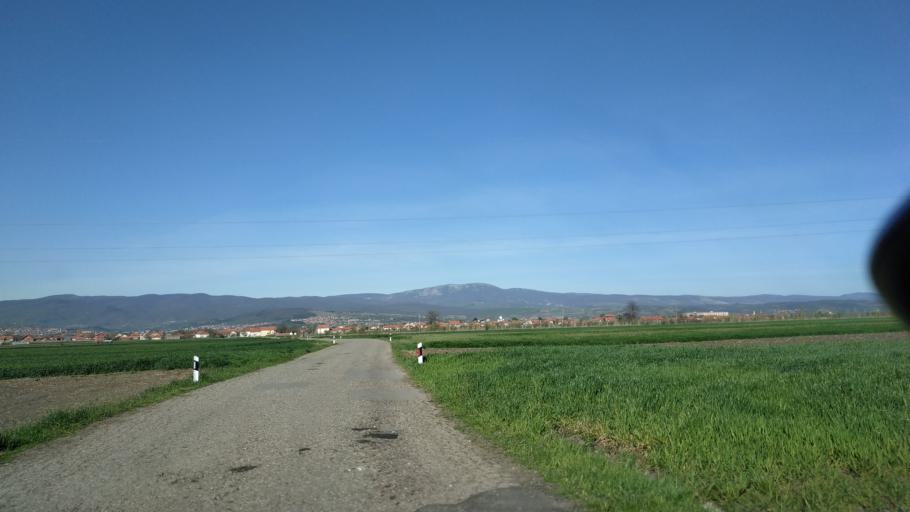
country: RS
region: Central Serbia
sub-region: Nisavski Okrug
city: Aleksinac
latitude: 43.5020
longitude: 21.6787
